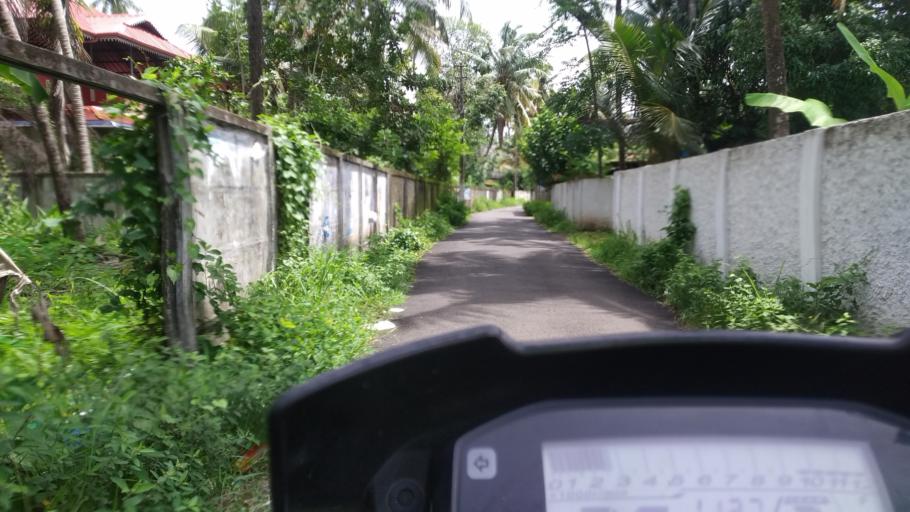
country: IN
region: Kerala
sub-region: Ernakulam
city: Elur
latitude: 10.0830
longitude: 76.2116
